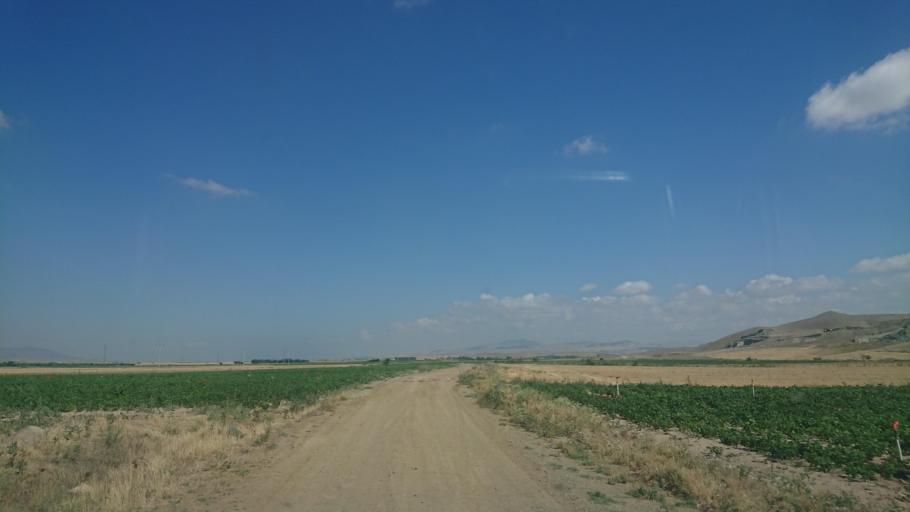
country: TR
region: Aksaray
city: Sariyahsi
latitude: 38.9749
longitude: 33.9141
